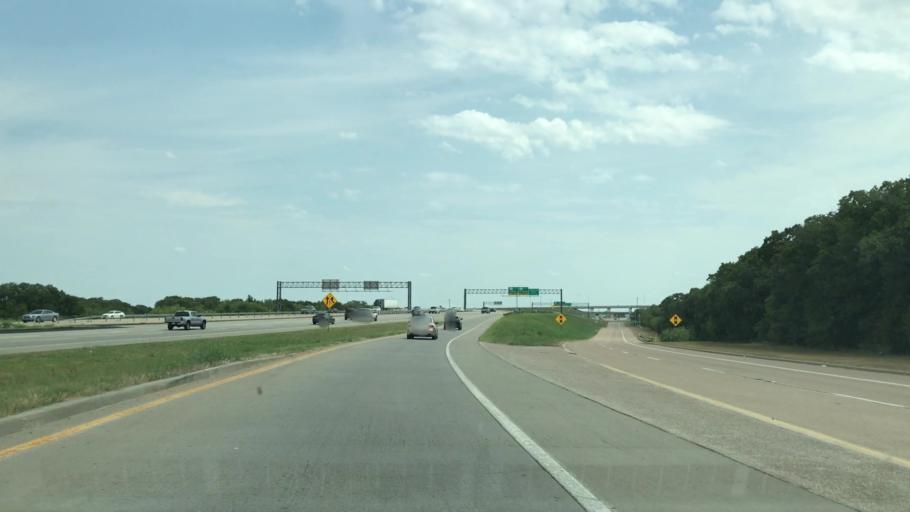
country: US
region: Texas
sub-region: Tarrant County
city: Euless
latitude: 32.8492
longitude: -97.0641
